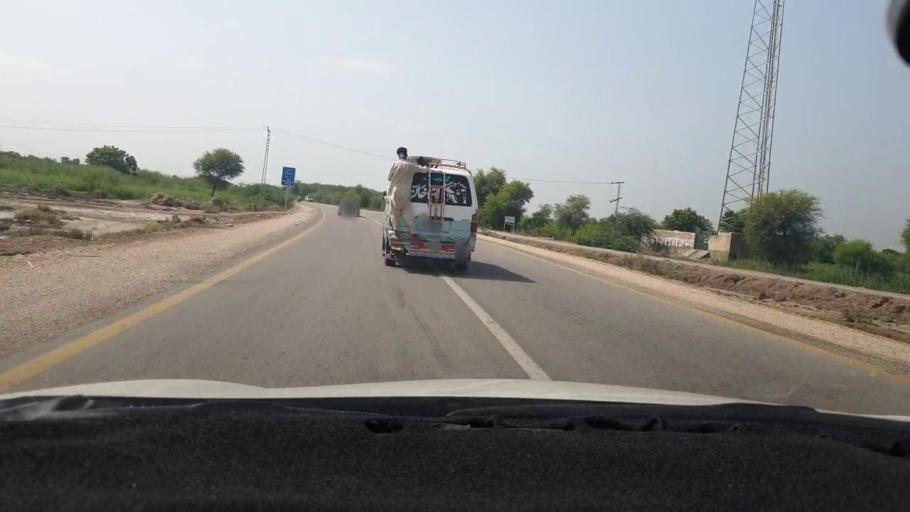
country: PK
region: Sindh
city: Mirpur Khas
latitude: 25.6166
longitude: 69.0830
